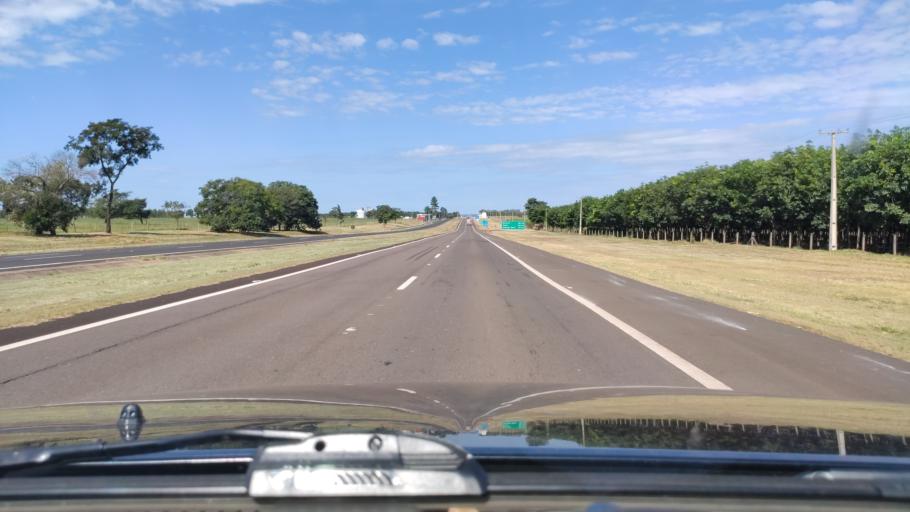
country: BR
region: Sao Paulo
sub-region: Rancharia
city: Rancharia
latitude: -22.4464
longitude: -50.9895
